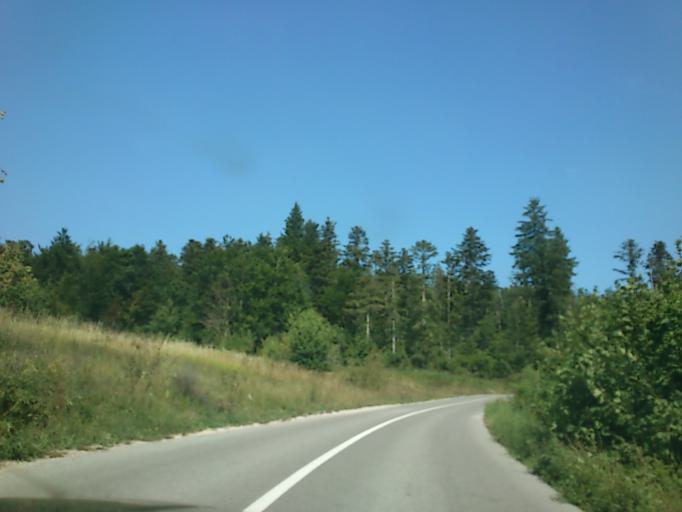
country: HR
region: Licko-Senjska
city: Otocac
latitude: 44.8210
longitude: 15.1063
